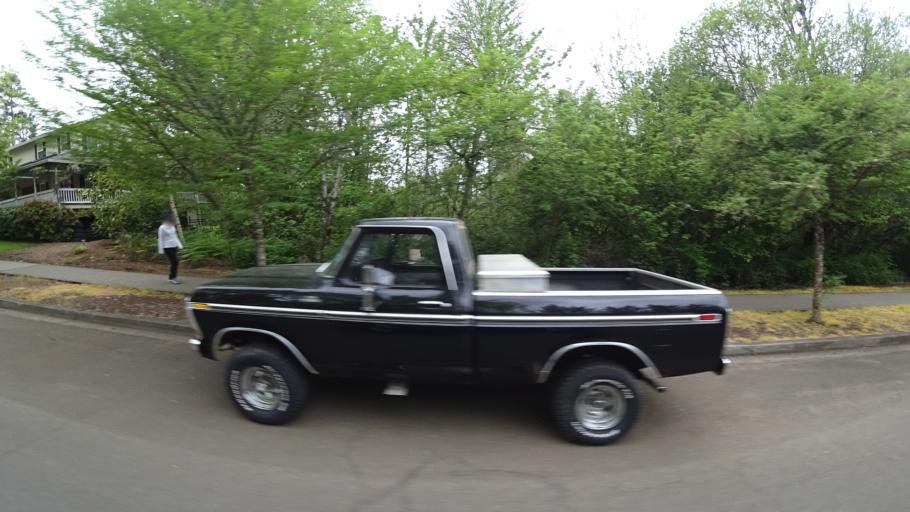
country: US
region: Oregon
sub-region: Washington County
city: Hillsboro
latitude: 45.5458
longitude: -122.9826
